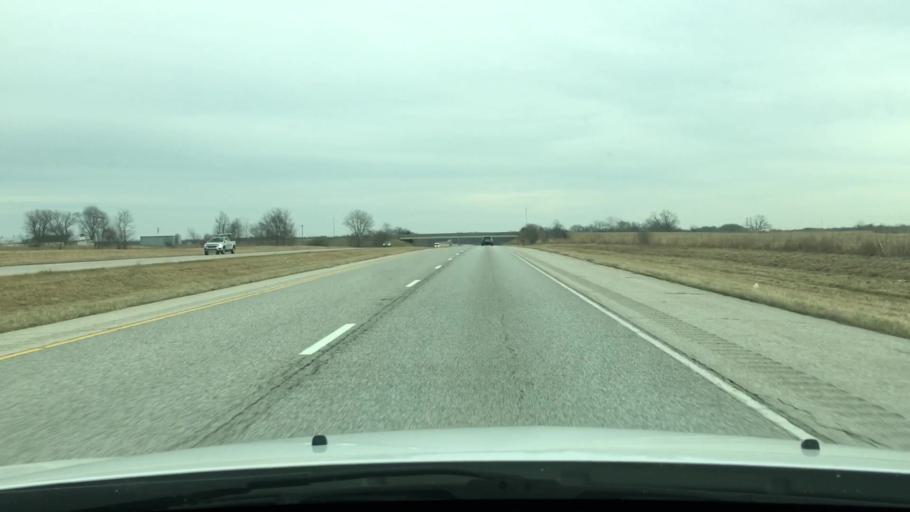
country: US
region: Illinois
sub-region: Pike County
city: Griggsville
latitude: 39.6781
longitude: -90.7091
